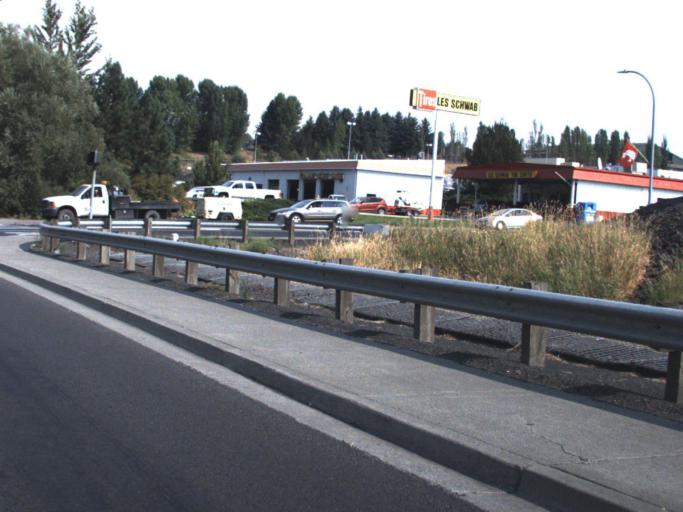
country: US
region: Washington
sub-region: Whitman County
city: Pullman
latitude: 46.7148
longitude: -117.1823
